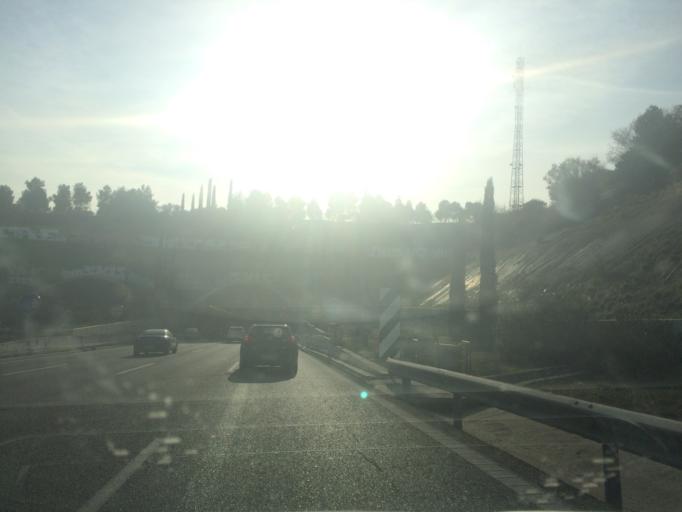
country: ES
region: Madrid
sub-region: Provincia de Madrid
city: Fuencarral-El Pardo
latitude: 40.4873
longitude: -3.7417
